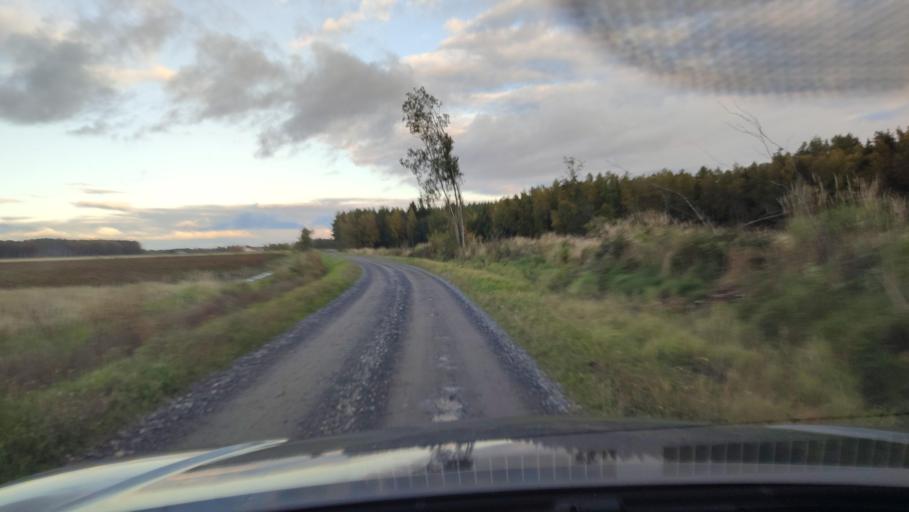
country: FI
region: Ostrobothnia
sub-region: Sydosterbotten
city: Kristinestad
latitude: 62.2511
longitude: 21.4592
